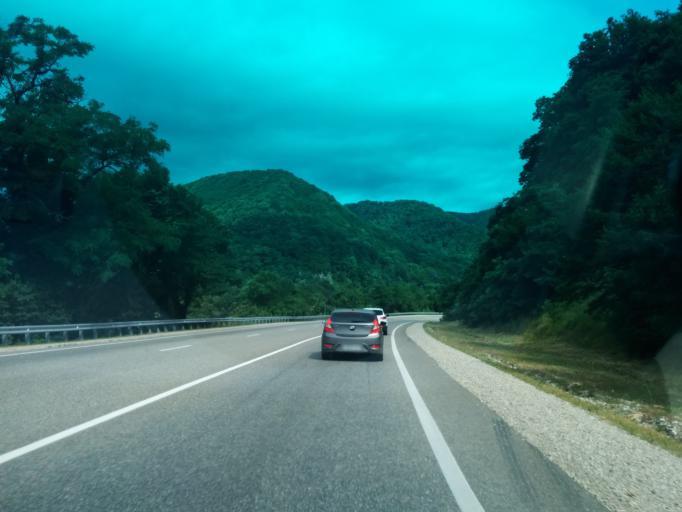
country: RU
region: Krasnodarskiy
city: Nebug
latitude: 44.1714
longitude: 38.9765
